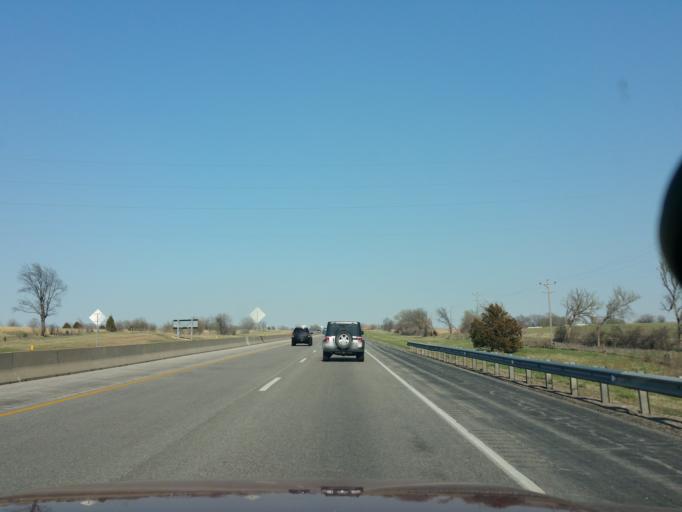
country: US
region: Kansas
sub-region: Leavenworth County
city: Basehor
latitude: 39.0722
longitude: -94.9976
